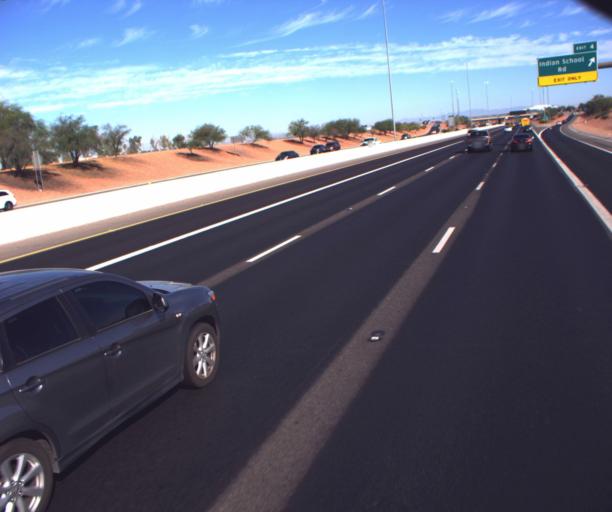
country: US
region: Arizona
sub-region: Maricopa County
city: Tolleson
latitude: 33.4880
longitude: -112.2637
